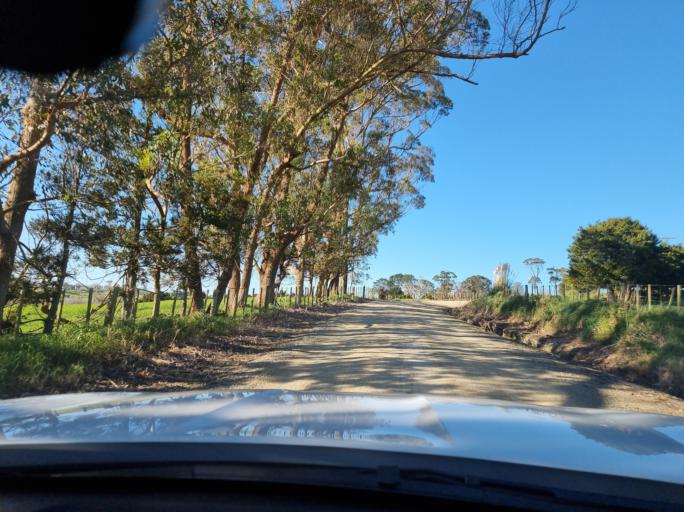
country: NZ
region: Auckland
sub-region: Auckland
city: Wellsford
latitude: -36.1657
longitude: 174.4379
